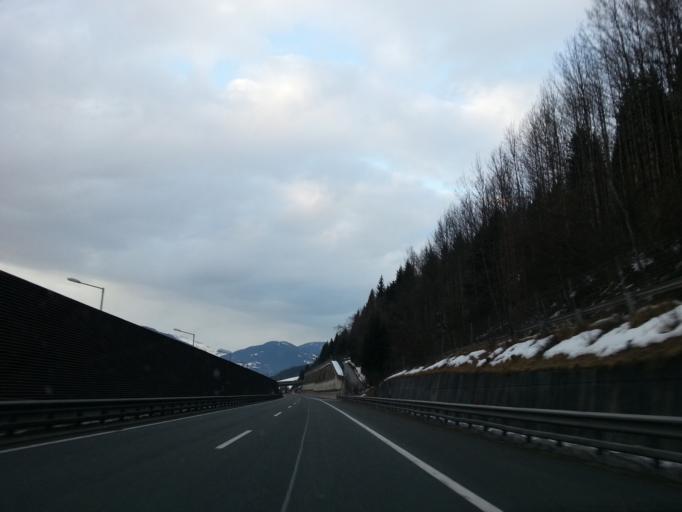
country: AT
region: Salzburg
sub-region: Politischer Bezirk Sankt Johann im Pongau
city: Flachau
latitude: 47.3468
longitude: 13.3970
